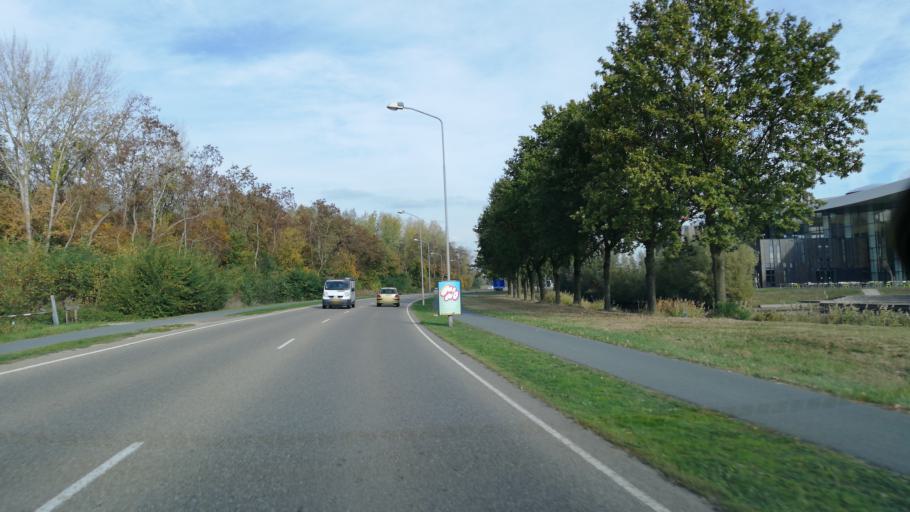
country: NL
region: Gelderland
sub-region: Gemeente Westervoort
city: Westervoort
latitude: 51.9647
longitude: 5.9845
